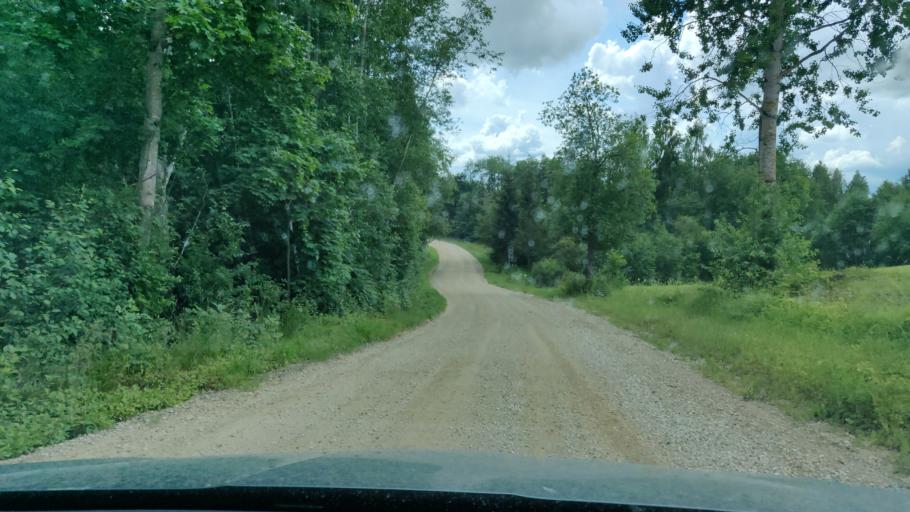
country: EE
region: Vorumaa
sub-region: Antsla vald
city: Vana-Antsla
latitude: 58.0382
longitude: 26.5547
